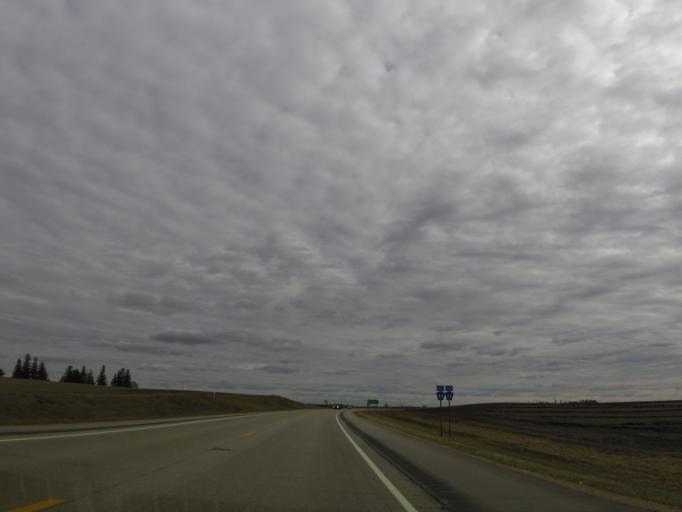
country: US
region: Minnesota
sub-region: Fillmore County
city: Spring Valley
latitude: 43.5463
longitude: -92.3732
